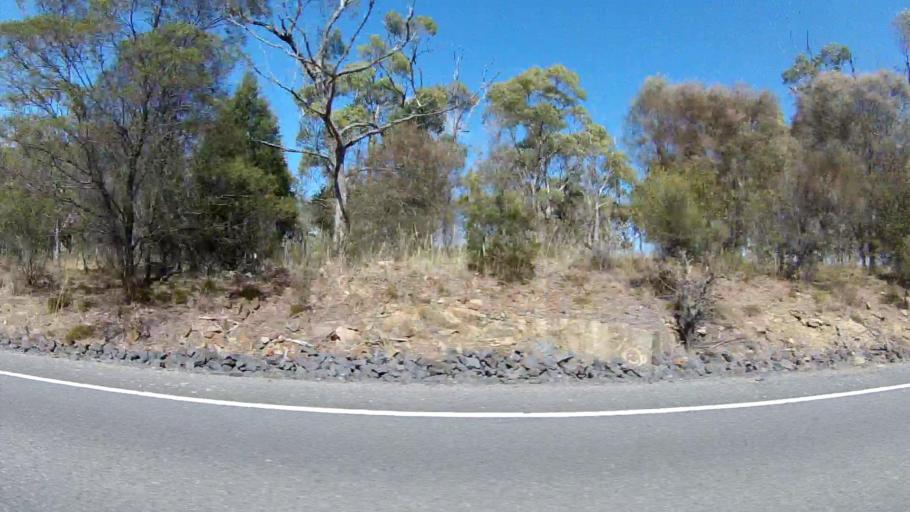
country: AU
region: Tasmania
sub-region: Sorell
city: Sorell
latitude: -42.5855
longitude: 147.8042
